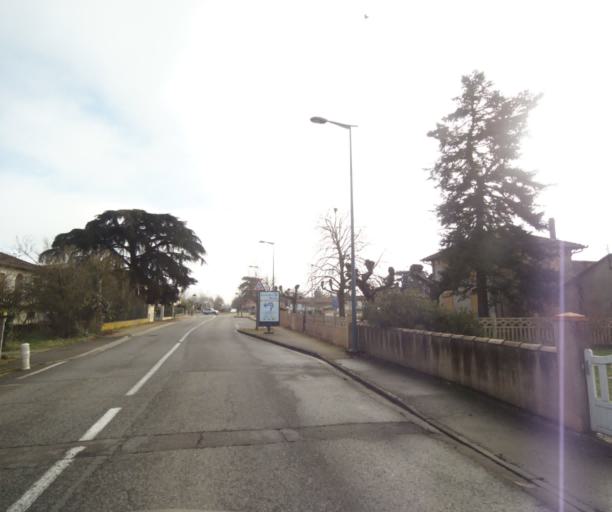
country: FR
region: Midi-Pyrenees
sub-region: Departement de la Haute-Garonne
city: Villemur-sur-Tarn
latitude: 43.8603
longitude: 1.4821
